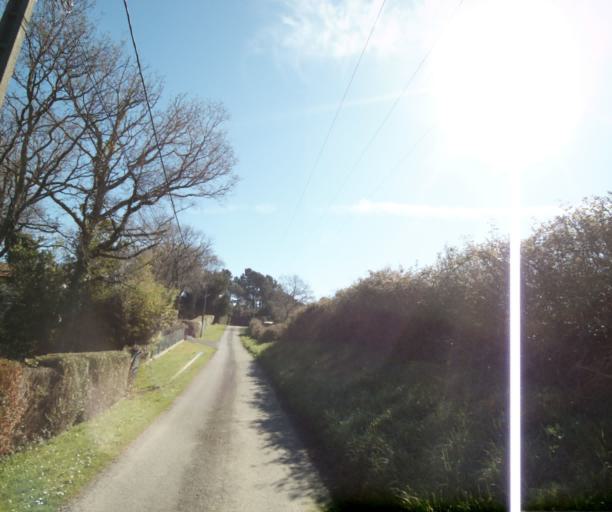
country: FR
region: Aquitaine
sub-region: Departement des Pyrenees-Atlantiques
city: Ciboure
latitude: 43.3631
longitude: -1.6725
